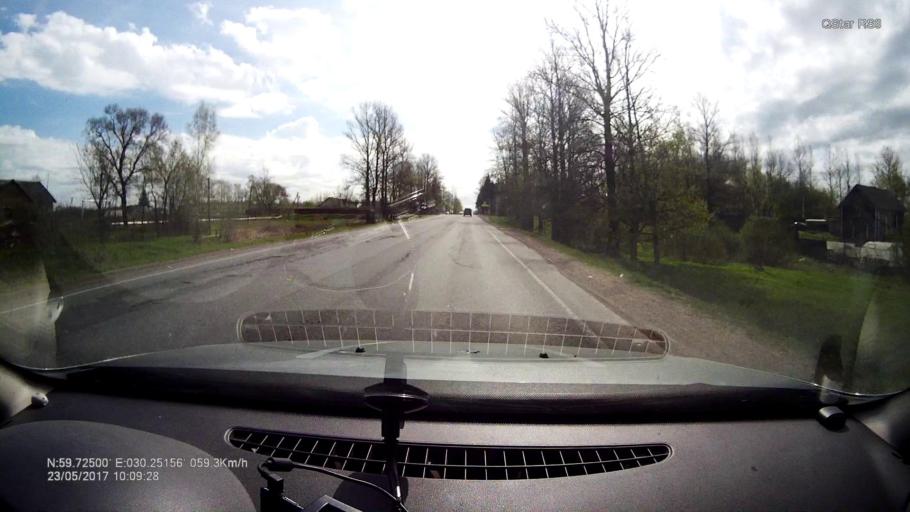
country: RU
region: St.-Petersburg
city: Aleksandrovskaya
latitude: 59.7250
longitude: 30.2518
